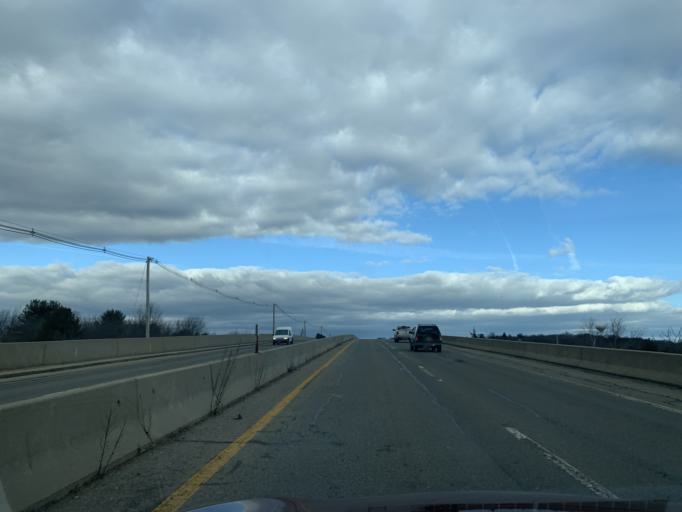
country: US
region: Massachusetts
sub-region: Essex County
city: Newburyport
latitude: 42.7931
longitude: -70.8774
